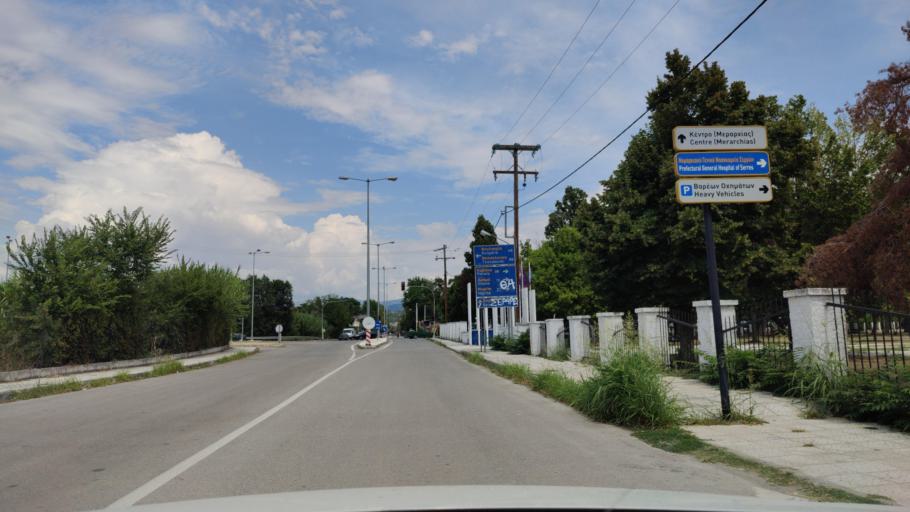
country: GR
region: Central Macedonia
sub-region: Nomos Serron
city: Serres
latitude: 41.0751
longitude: 23.5372
